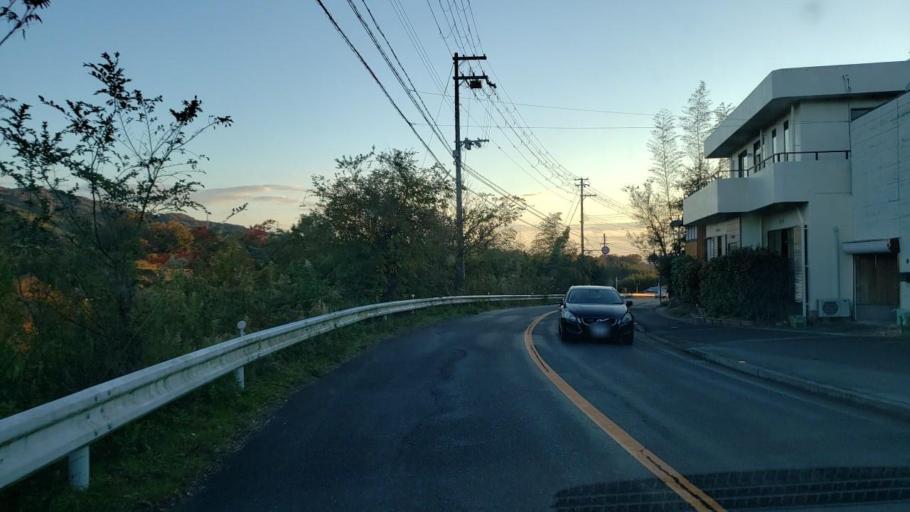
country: JP
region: Hyogo
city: Sumoto
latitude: 34.3869
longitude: 134.8085
